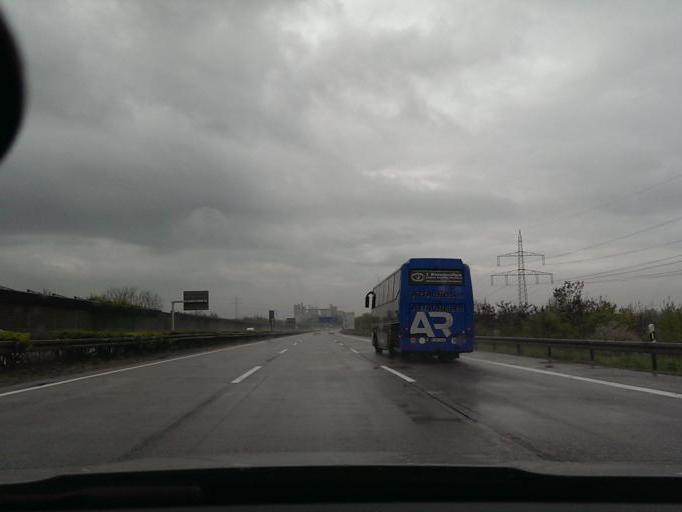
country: DE
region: Lower Saxony
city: Lehrte
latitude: 52.3728
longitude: 9.8950
